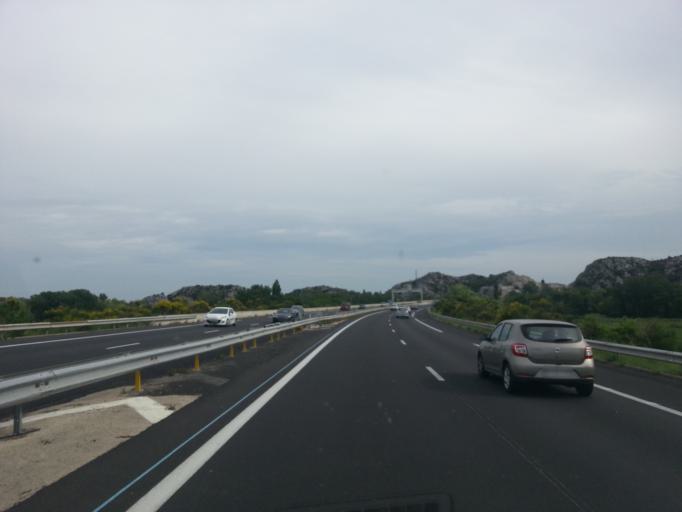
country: FR
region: Languedoc-Roussillon
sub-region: Departement du Gard
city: Roquemaure
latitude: 44.0595
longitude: 4.7673
